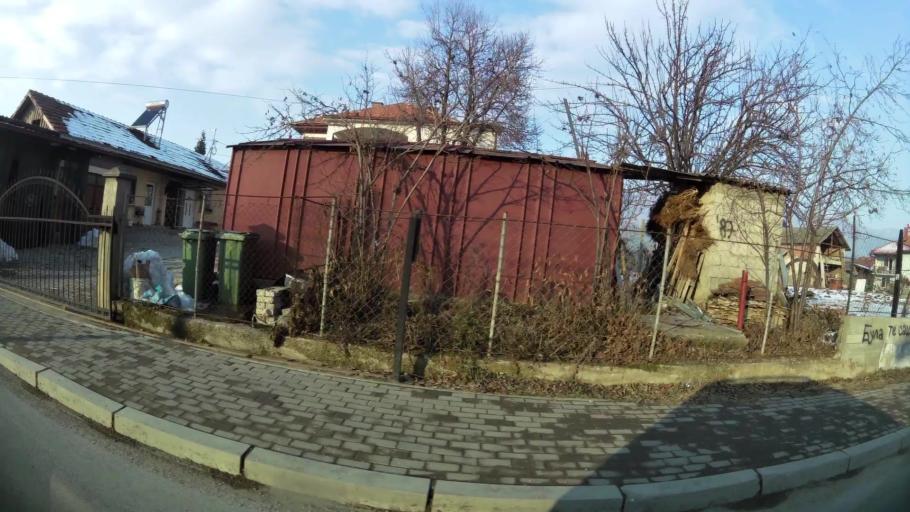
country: MK
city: Creshevo
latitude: 42.0279
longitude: 21.5168
